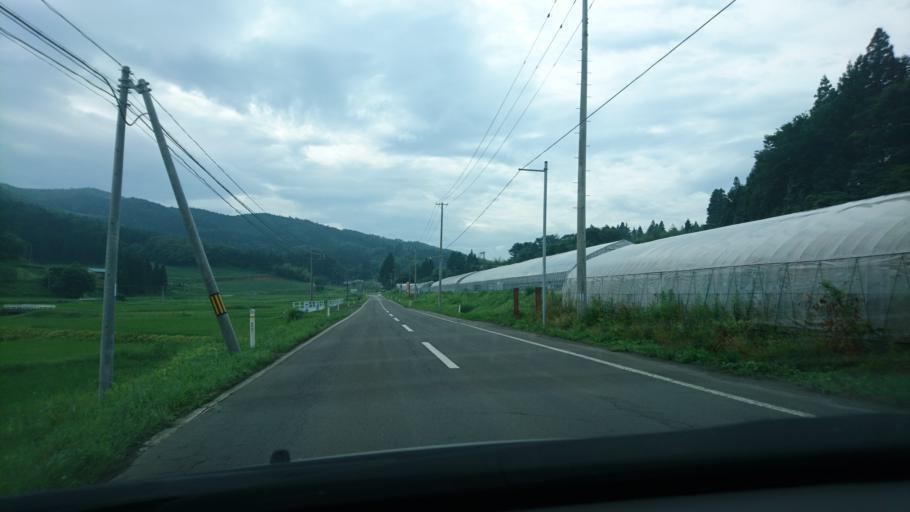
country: JP
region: Iwate
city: Ichinoseki
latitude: 38.9273
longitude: 141.4199
